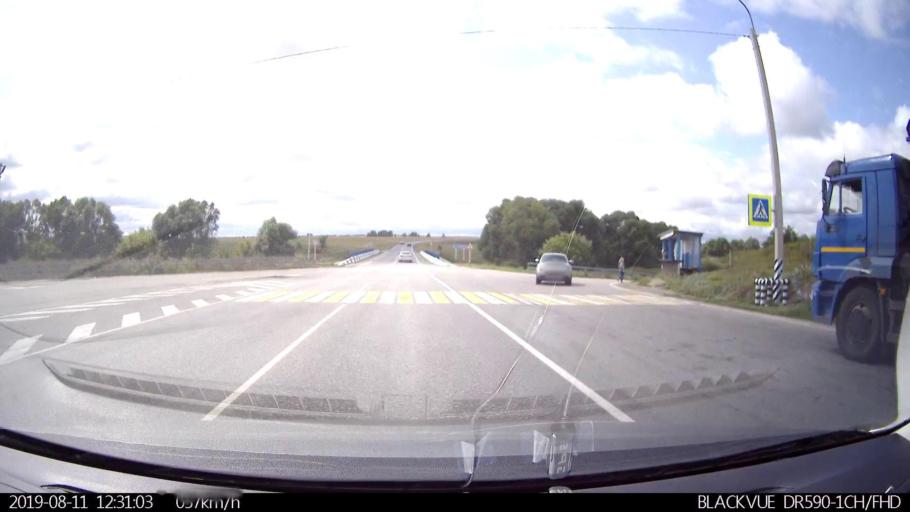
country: RU
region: Ulyanovsk
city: Ignatovka
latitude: 53.8219
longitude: 47.8886
